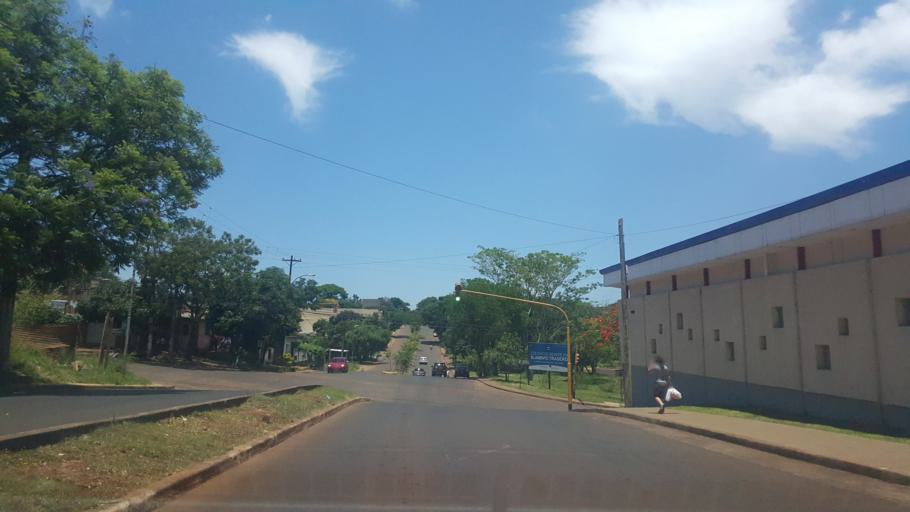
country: AR
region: Misiones
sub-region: Departamento de Capital
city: Posadas
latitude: -27.3660
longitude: -55.9392
